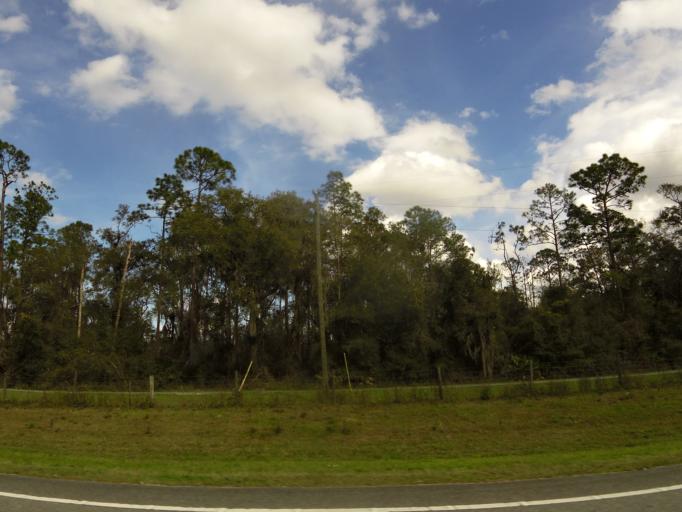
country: US
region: Florida
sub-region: Volusia County
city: De Leon Springs
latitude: 29.2285
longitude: -81.3234
